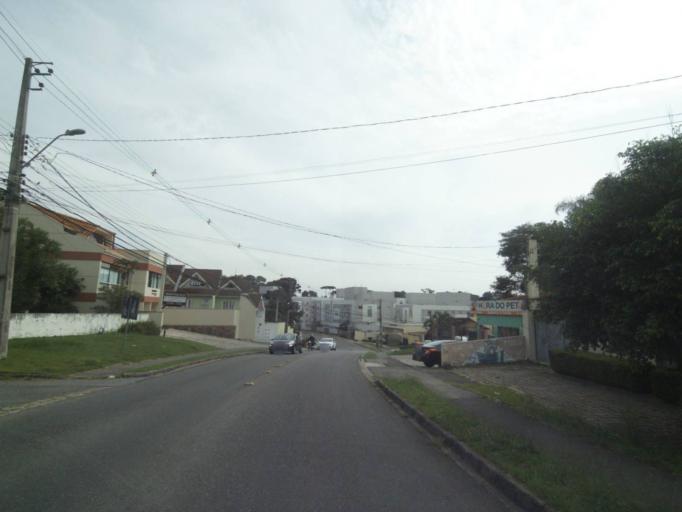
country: BR
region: Parana
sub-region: Curitiba
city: Curitiba
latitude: -25.4132
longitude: -49.2942
